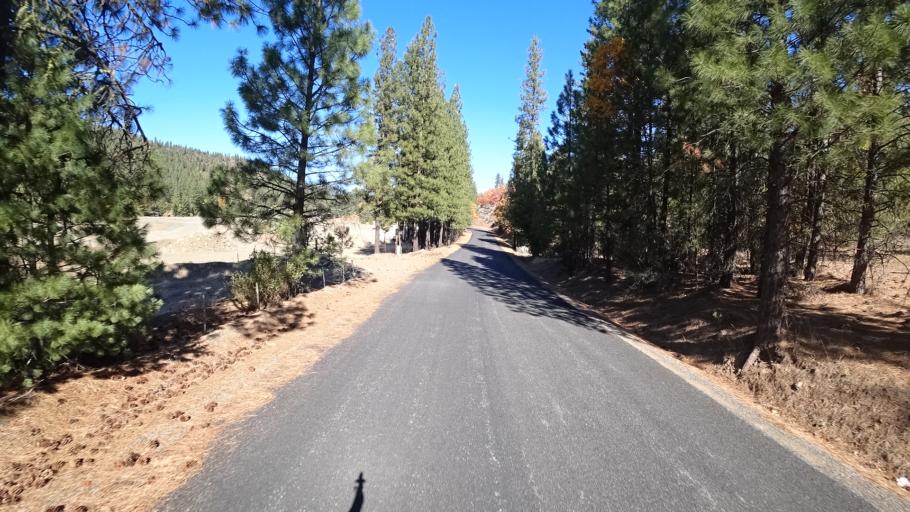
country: US
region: California
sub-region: Siskiyou County
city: Yreka
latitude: 41.6646
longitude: -122.8510
